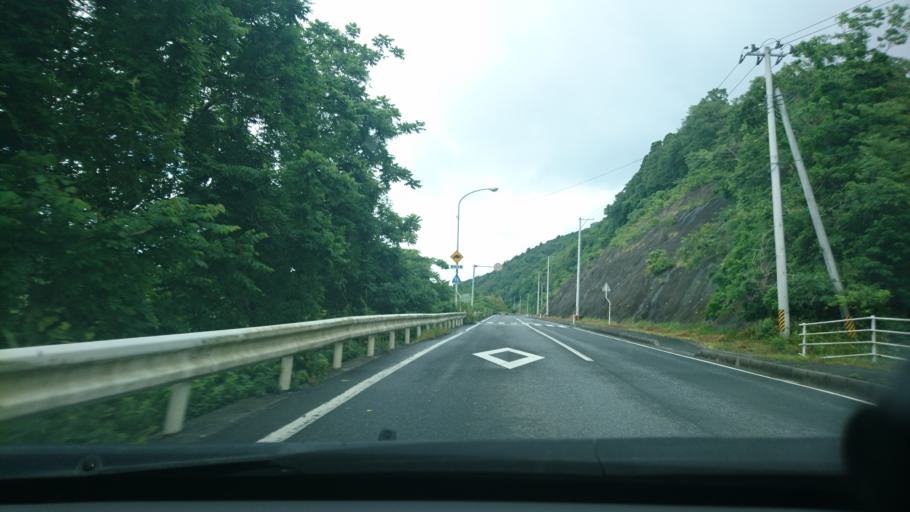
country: JP
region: Miyagi
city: Ishinomaki
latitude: 38.5659
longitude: 141.3002
